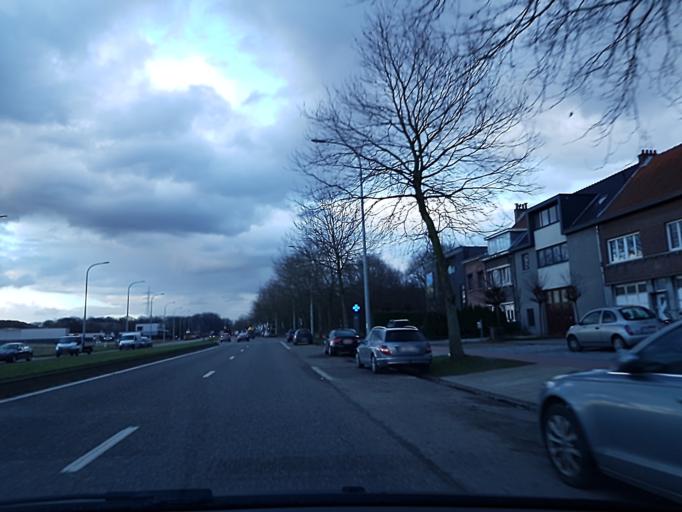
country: BE
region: Flanders
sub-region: Provincie Antwerpen
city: Schoten
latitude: 51.2362
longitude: 4.4809
